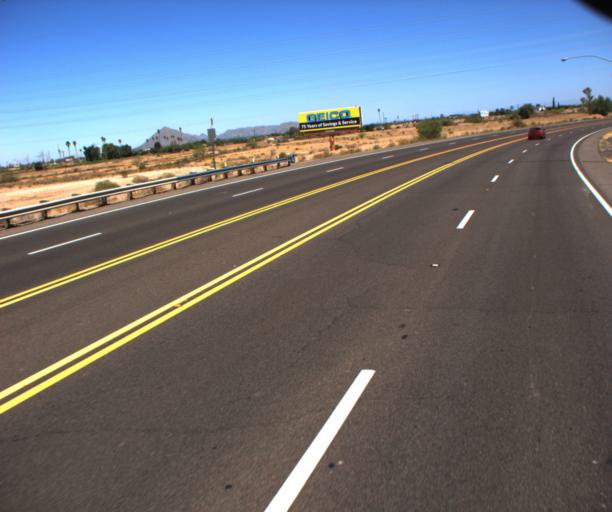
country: US
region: Arizona
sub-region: Maricopa County
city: Mesa
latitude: 33.4621
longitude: -111.8426
